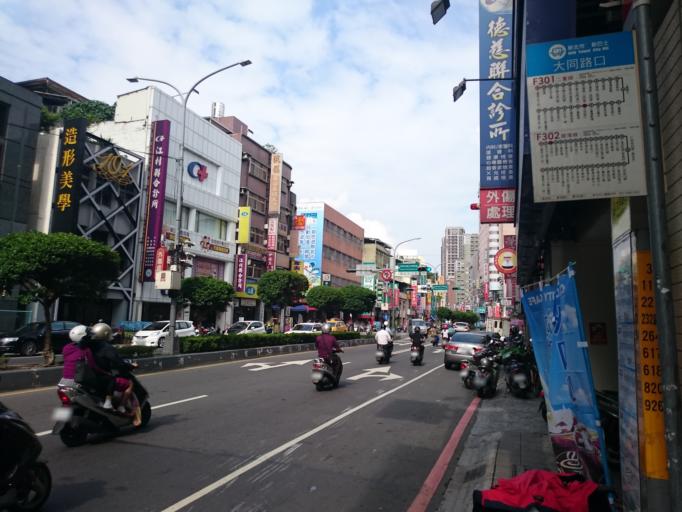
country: TW
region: Taipei
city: Taipei
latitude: 25.0614
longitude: 121.4950
